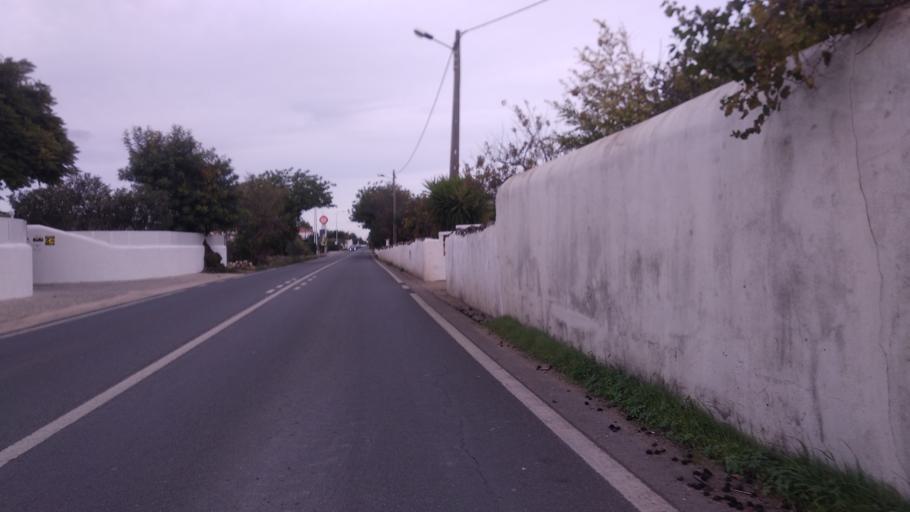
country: PT
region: Faro
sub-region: Faro
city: Santa Barbara de Nexe
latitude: 37.1507
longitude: -7.9419
